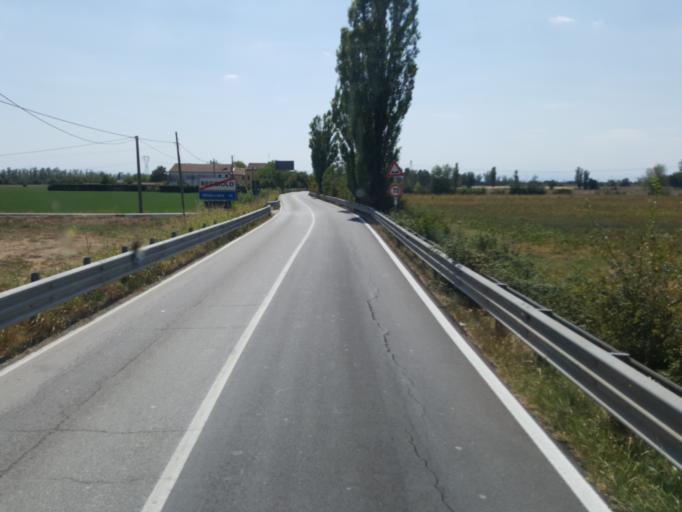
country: IT
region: Emilia-Romagna
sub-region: Provincia di Reggio Emilia
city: Reggiolo
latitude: 44.9088
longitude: 10.7979
